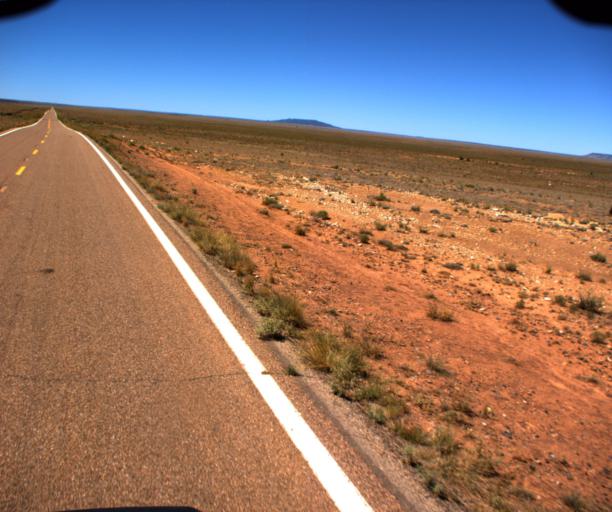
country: US
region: Arizona
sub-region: Navajo County
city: Winslow
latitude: 34.8572
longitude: -110.6634
